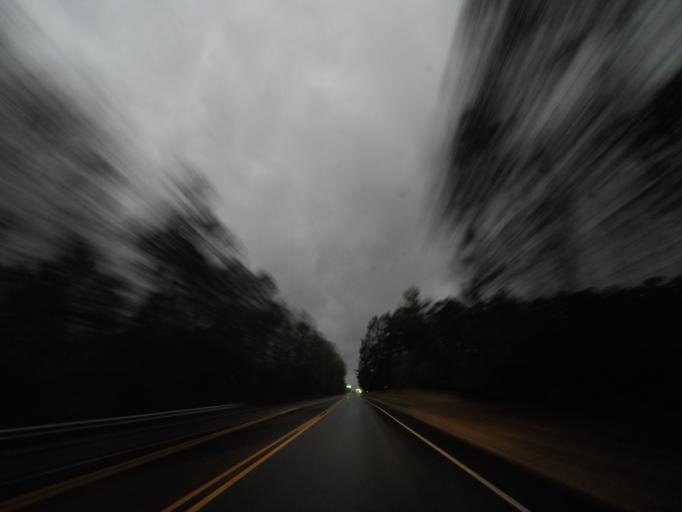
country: US
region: North Carolina
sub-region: Orange County
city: Hillsborough
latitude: 36.0855
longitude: -79.0945
